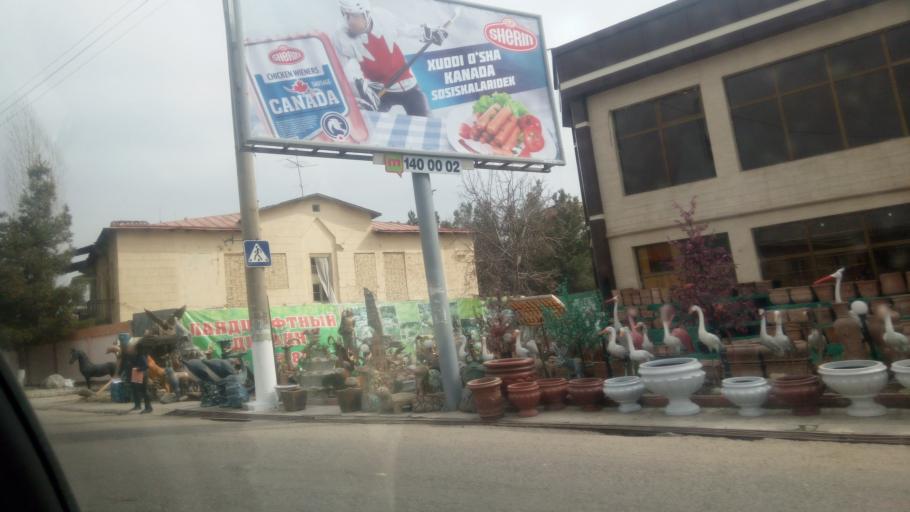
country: UZ
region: Toshkent
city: Salor
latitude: 41.3322
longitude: 69.2945
